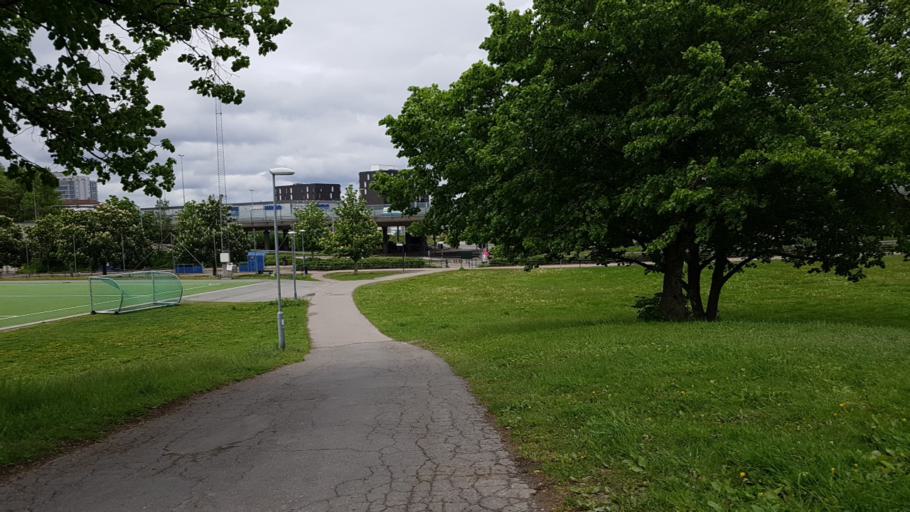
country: NO
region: Oslo
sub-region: Oslo
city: Oslo
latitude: 59.9400
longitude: 10.7841
